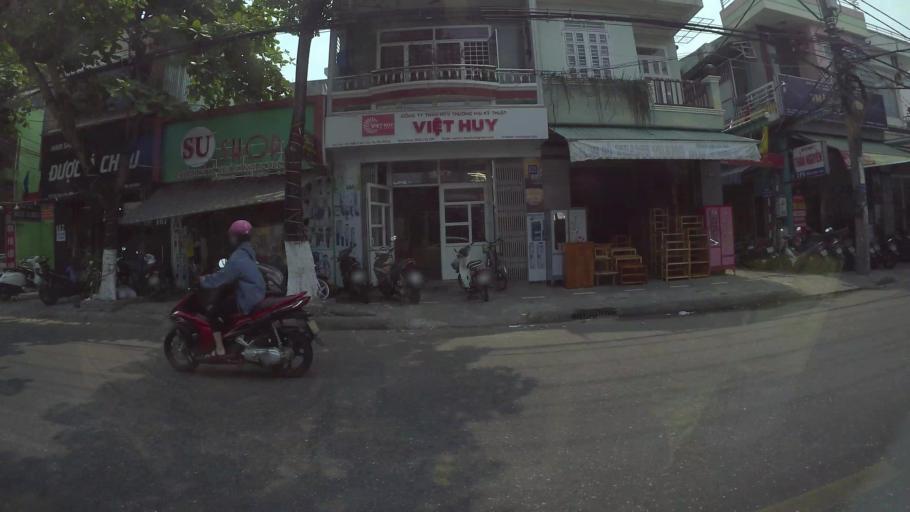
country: VN
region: Da Nang
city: Thanh Khe
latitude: 16.0714
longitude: 108.2027
